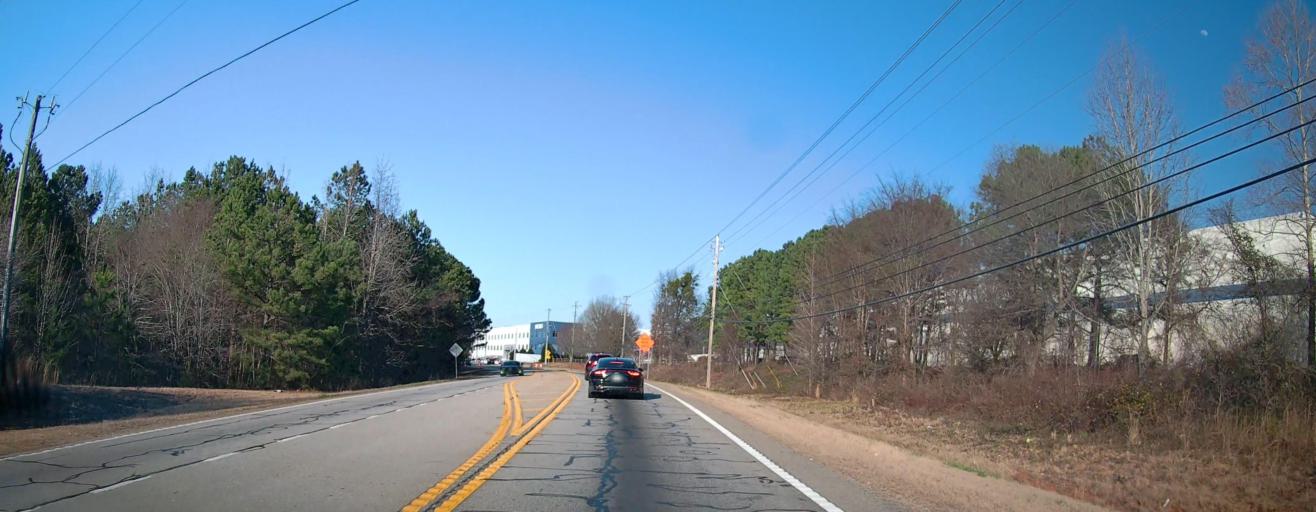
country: US
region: Georgia
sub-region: Henry County
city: McDonough
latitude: 33.3880
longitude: -84.1744
